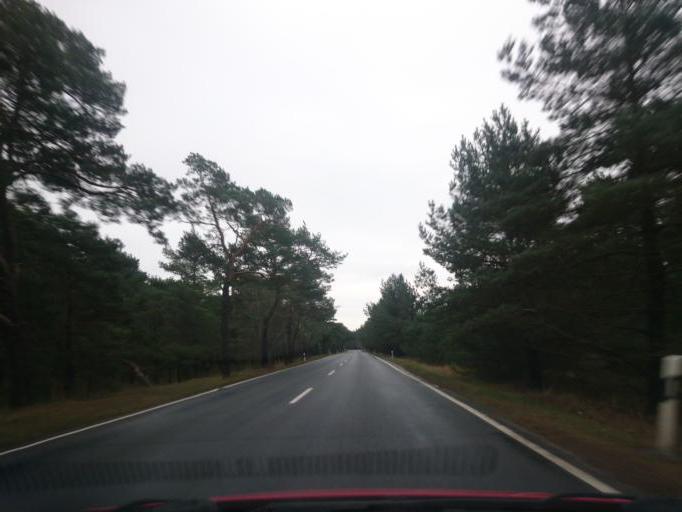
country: DE
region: Mecklenburg-Vorpommern
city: Glowe
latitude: 54.5883
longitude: 13.3984
